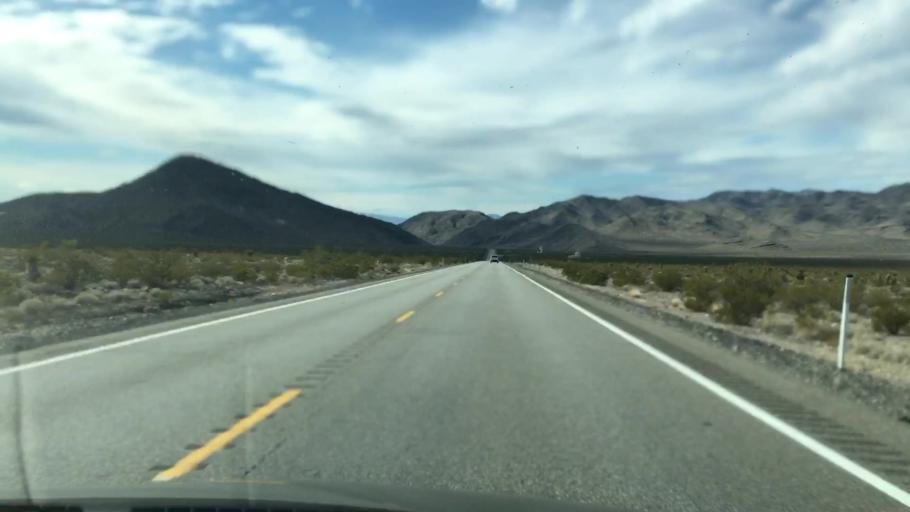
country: US
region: Nevada
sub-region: Nye County
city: Pahrump
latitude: 36.5931
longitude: -116.0250
